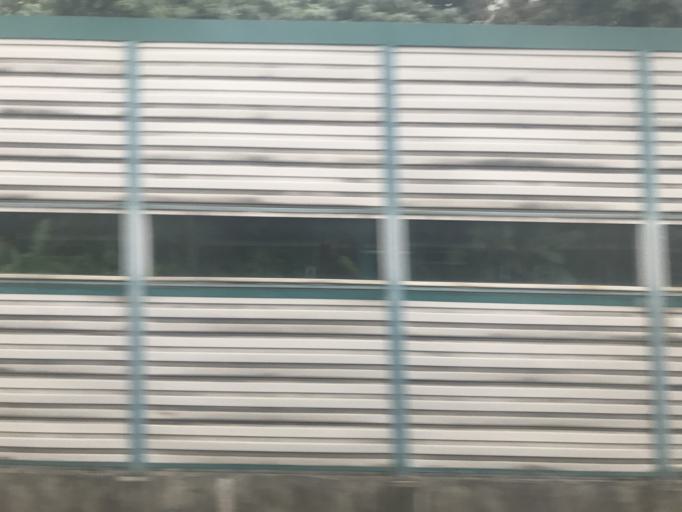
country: HK
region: Kowloon City
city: Kowloon
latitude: 22.3308
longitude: 114.1764
